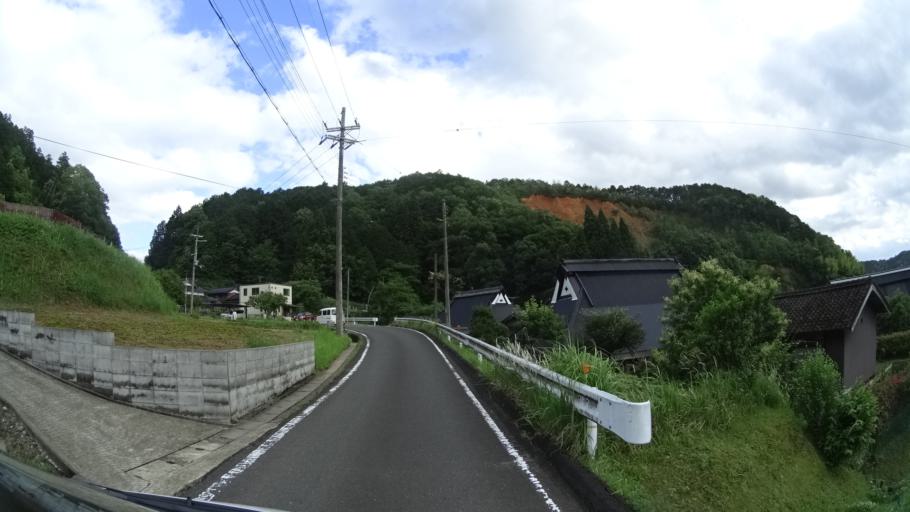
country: JP
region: Kyoto
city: Ayabe
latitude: 35.3670
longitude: 135.2437
